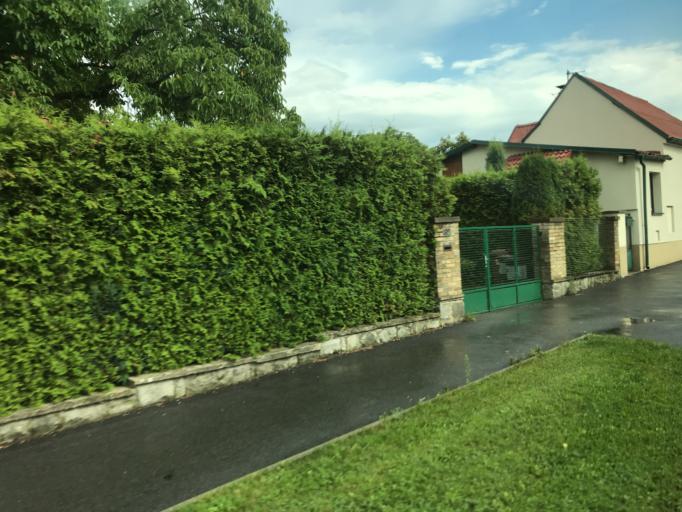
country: CZ
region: Jihocesky
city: Vcelna
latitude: 48.9221
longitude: 14.4533
